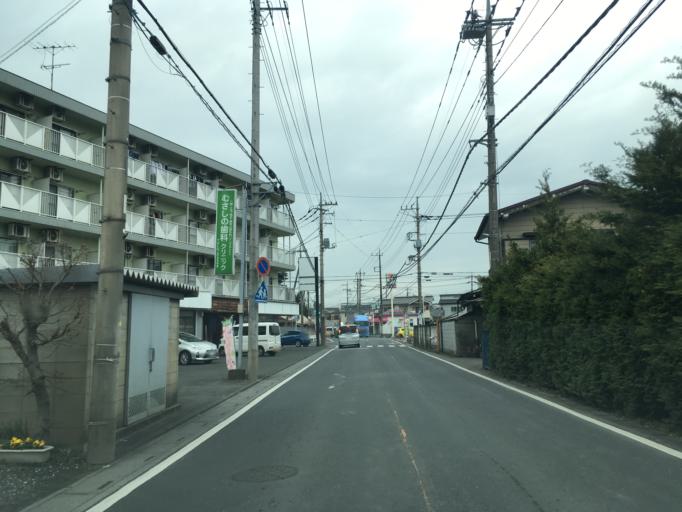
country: JP
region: Saitama
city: Hanno
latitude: 35.8462
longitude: 139.3209
